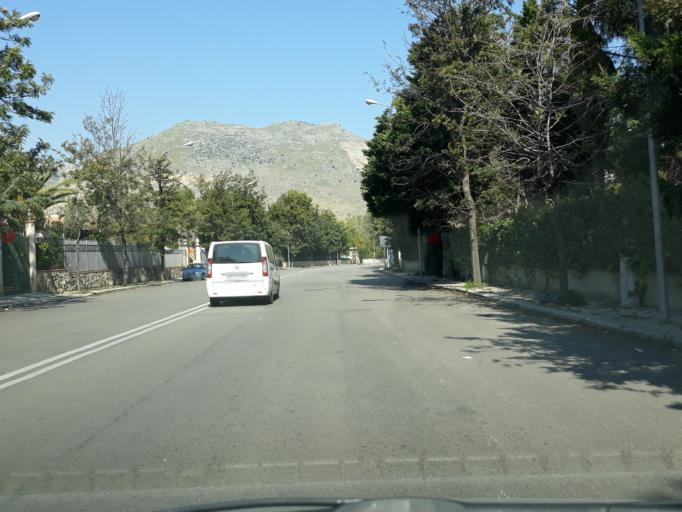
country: IT
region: Sicily
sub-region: Palermo
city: Palermo
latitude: 38.1233
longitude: 13.3036
